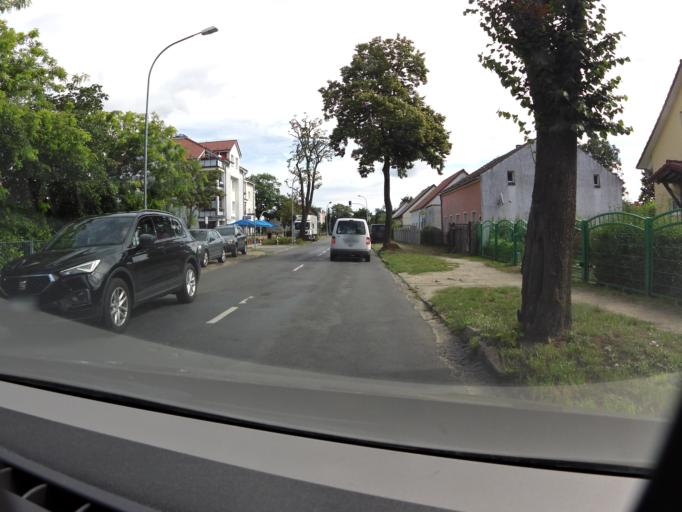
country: DE
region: Brandenburg
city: Furstenwalde
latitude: 52.3504
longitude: 14.0550
